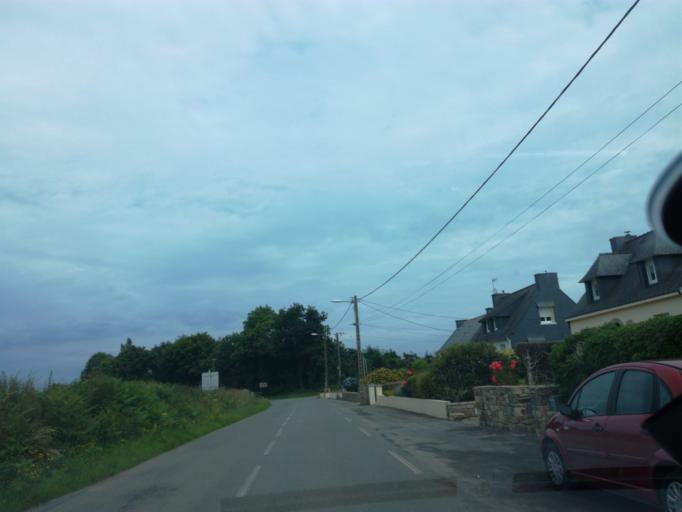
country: FR
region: Brittany
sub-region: Departement du Morbihan
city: Saint-Thuriau
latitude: 48.0121
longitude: -2.9451
